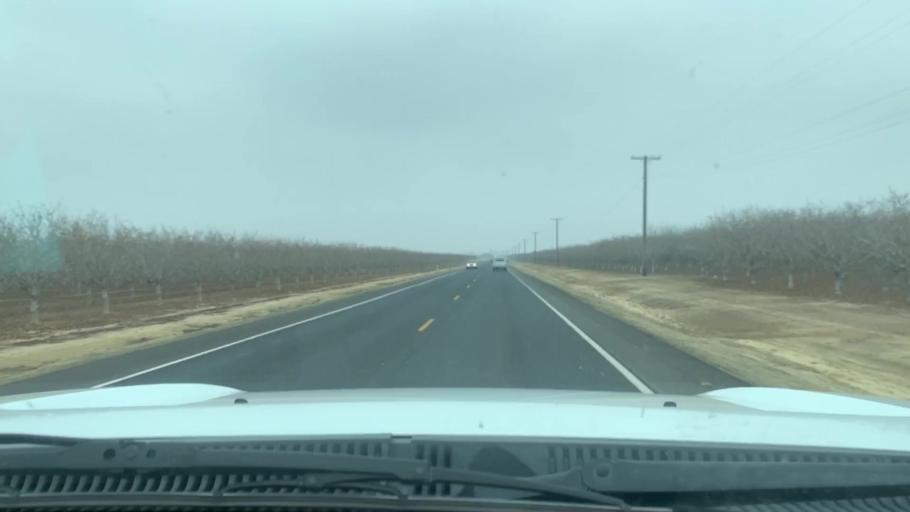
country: US
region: California
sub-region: Kern County
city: Lost Hills
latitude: 35.4993
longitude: -119.6338
